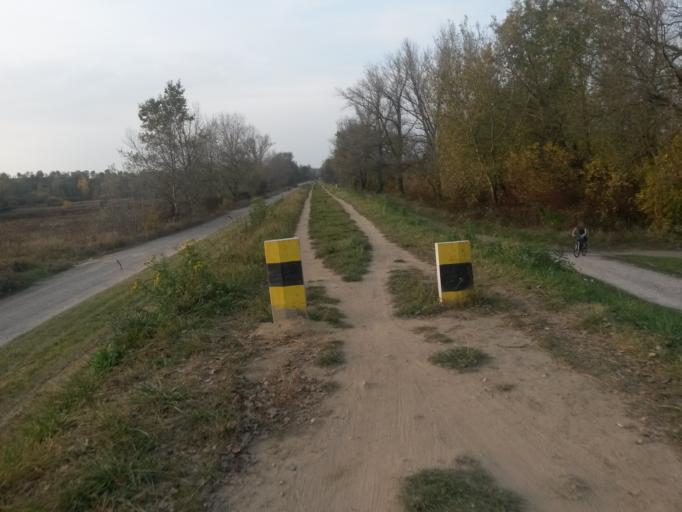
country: PL
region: Masovian Voivodeship
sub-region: Warszawa
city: Wawer
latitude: 52.1440
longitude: 21.1544
